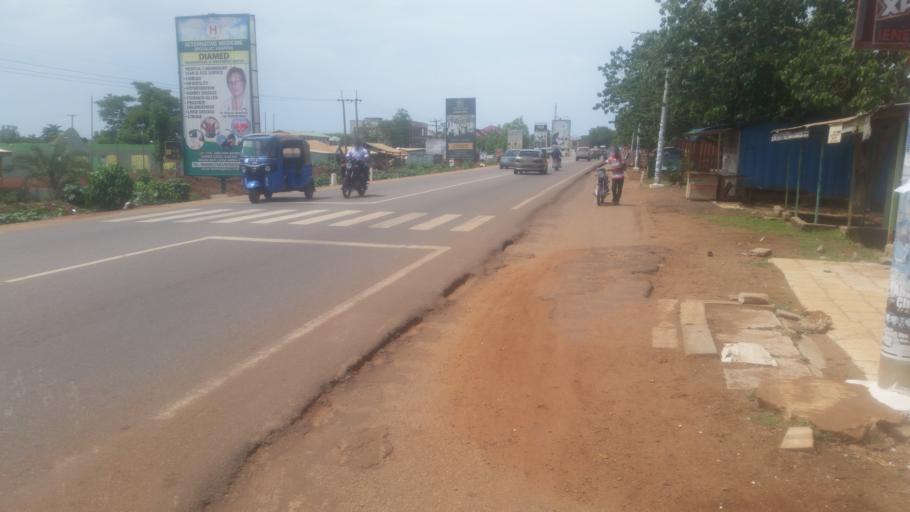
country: GH
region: Northern
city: Tamale
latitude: 9.4429
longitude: -0.8442
